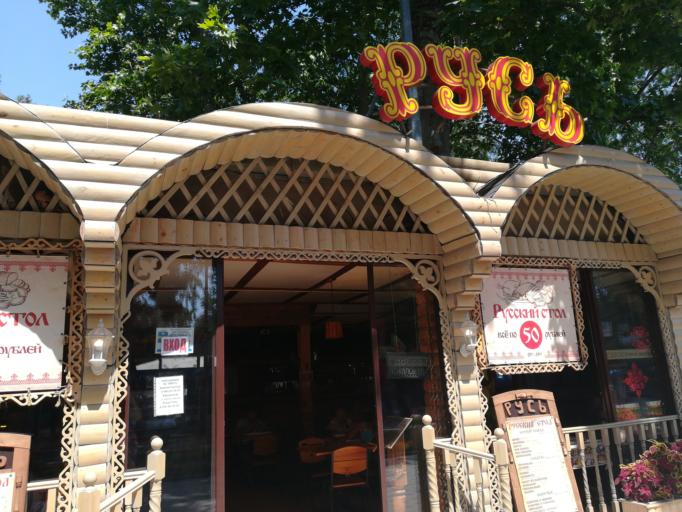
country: RU
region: Krasnodarskiy
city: Anapa
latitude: 44.8968
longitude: 37.3144
